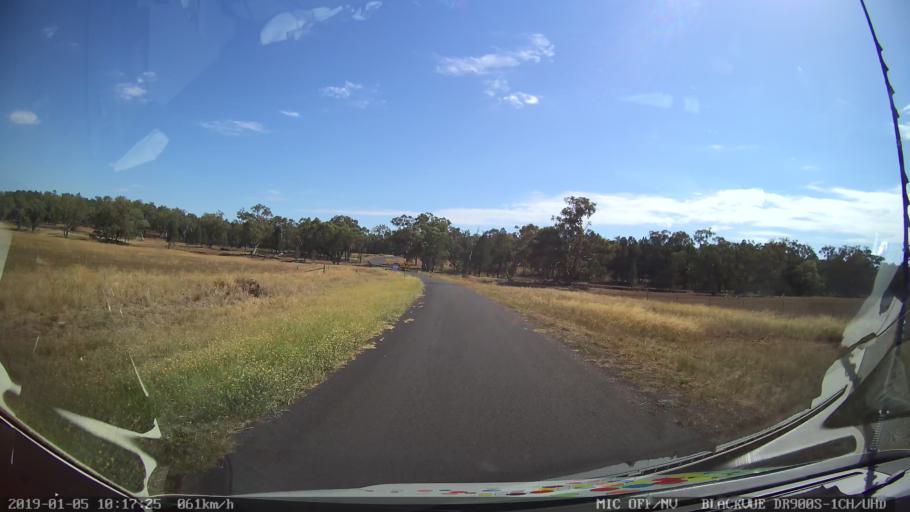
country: AU
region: New South Wales
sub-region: Gilgandra
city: Gilgandra
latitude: -31.5671
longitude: 148.9604
